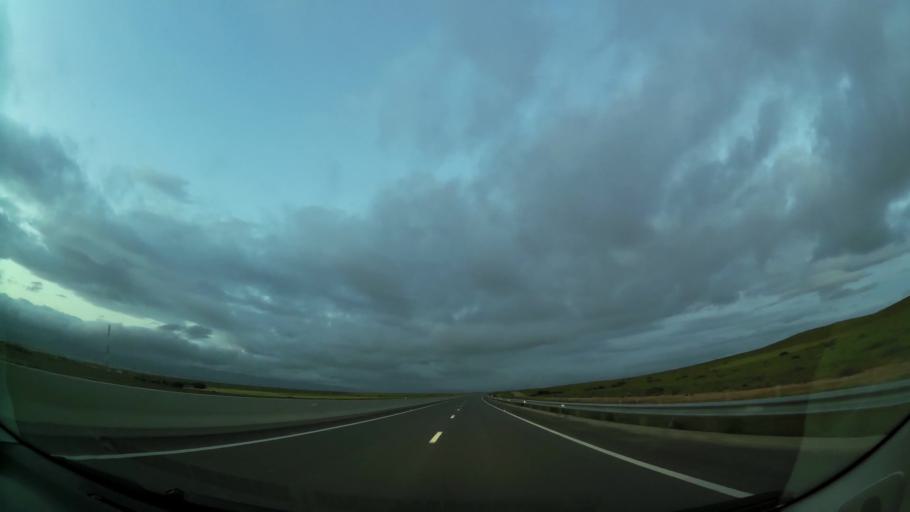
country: MA
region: Oriental
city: El Aioun
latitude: 34.6258
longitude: -2.3877
